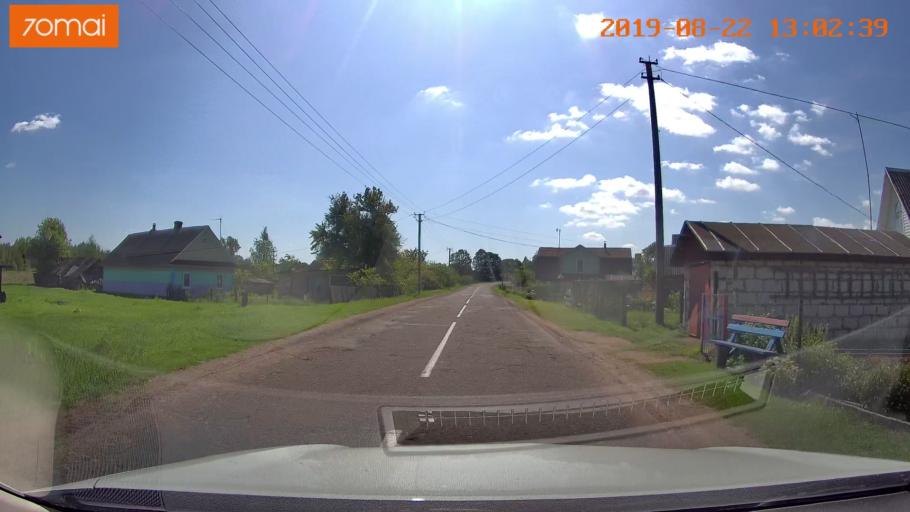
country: BY
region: Minsk
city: Prawdzinski
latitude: 53.3870
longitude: 27.8253
